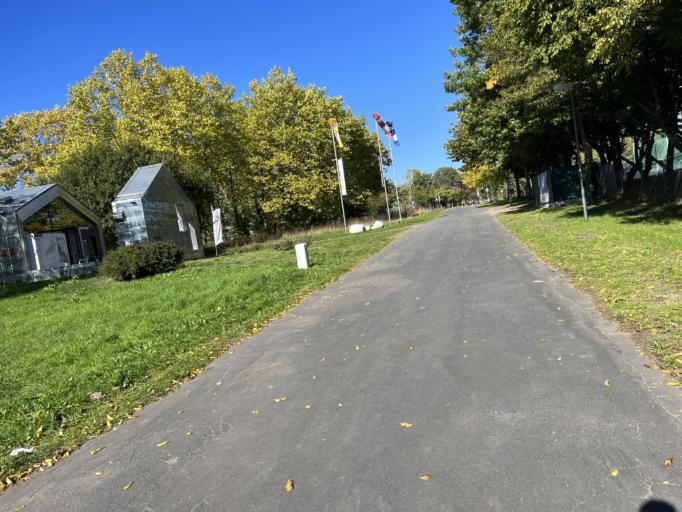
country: DE
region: Hesse
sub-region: Regierungsbezirk Darmstadt
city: Offenbach
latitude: 50.0890
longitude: 8.7859
